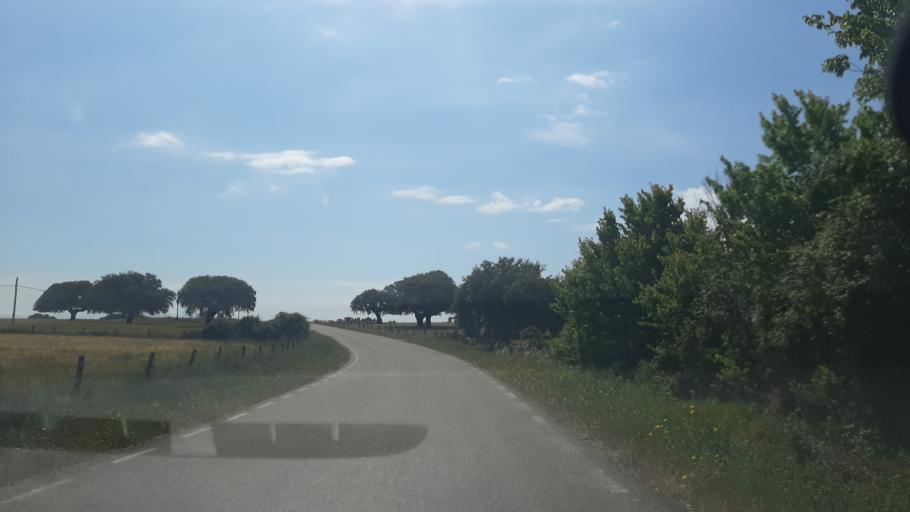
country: ES
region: Castille and Leon
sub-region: Provincia de Salamanca
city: Gallegos de Arganan
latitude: 40.6445
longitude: -6.7451
